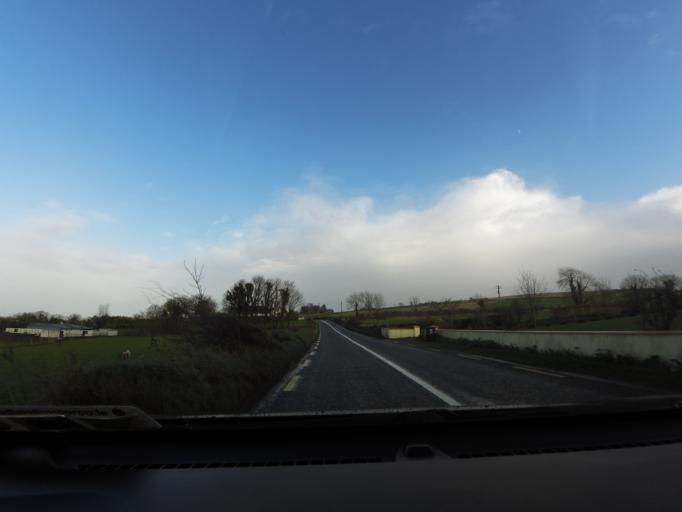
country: IE
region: Connaught
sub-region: County Galway
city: Tuam
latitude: 53.4893
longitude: -8.9496
